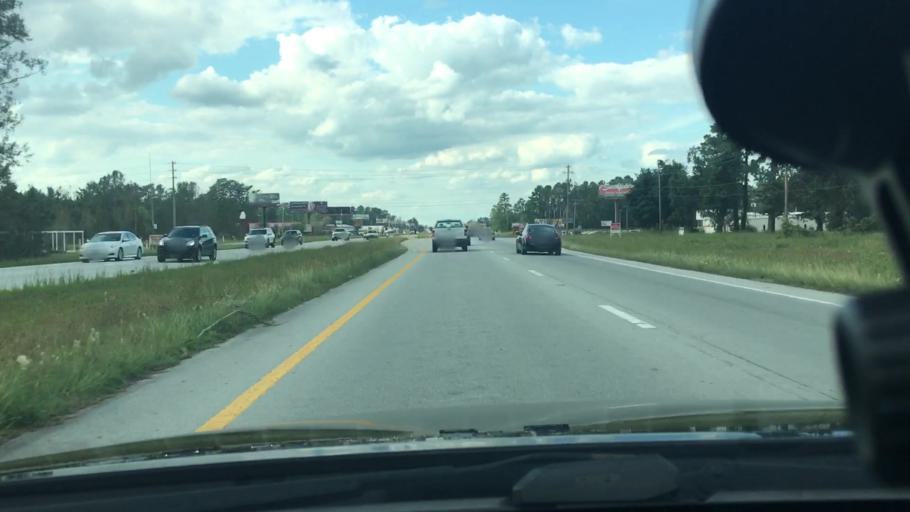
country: US
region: North Carolina
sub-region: Craven County
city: James City
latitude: 35.0550
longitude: -77.0171
